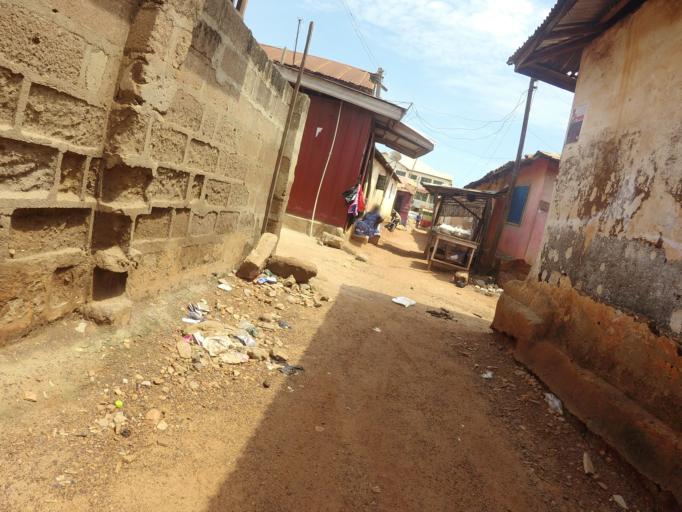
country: GH
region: Greater Accra
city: Accra
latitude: 5.5901
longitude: -0.2058
